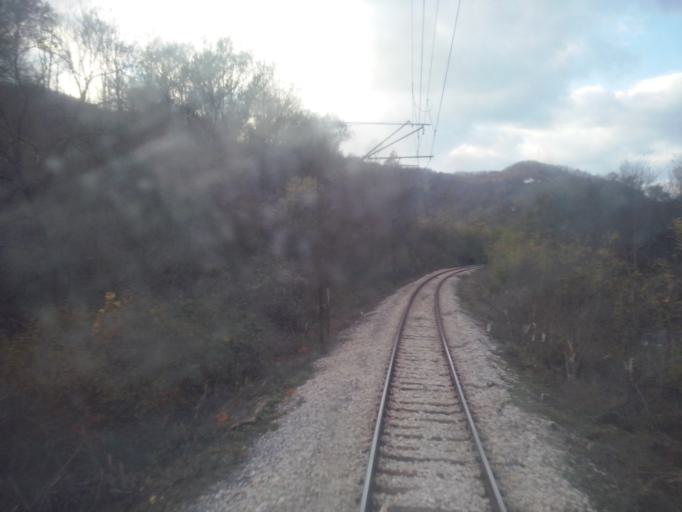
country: RS
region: Central Serbia
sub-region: Zlatiborski Okrug
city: Kosjeric
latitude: 43.9650
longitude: 19.9623
